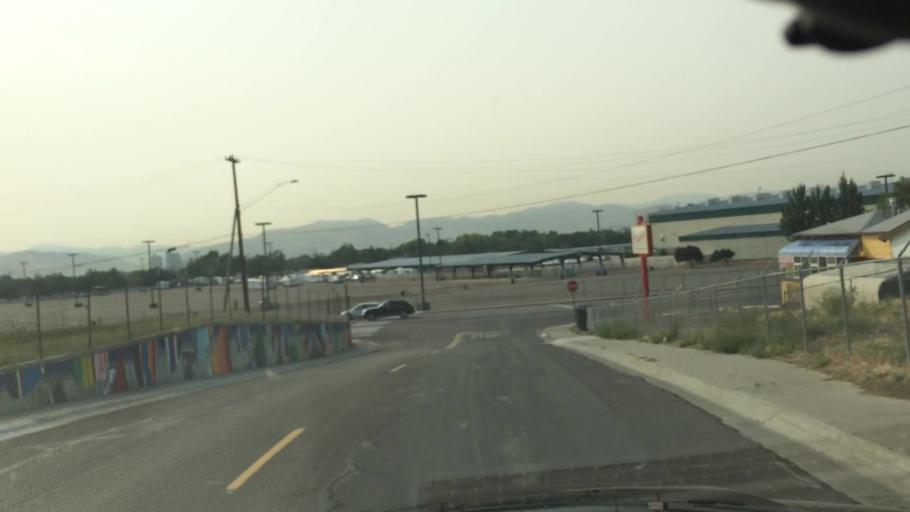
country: US
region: Nevada
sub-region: Washoe County
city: Reno
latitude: 39.5448
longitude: -119.8032
